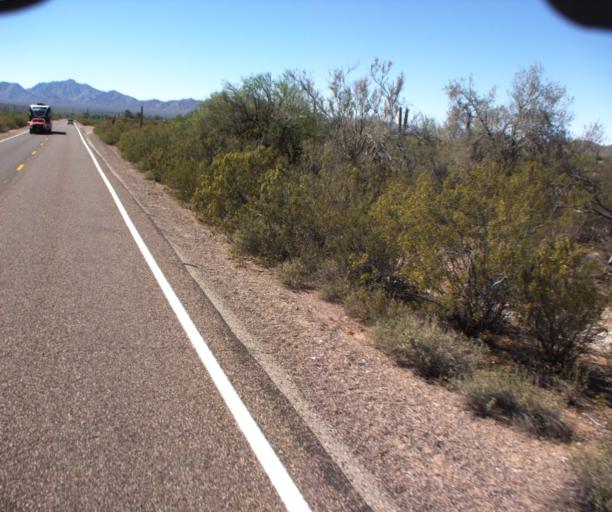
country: MX
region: Sonora
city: Sonoyta
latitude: 31.8954
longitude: -112.8120
